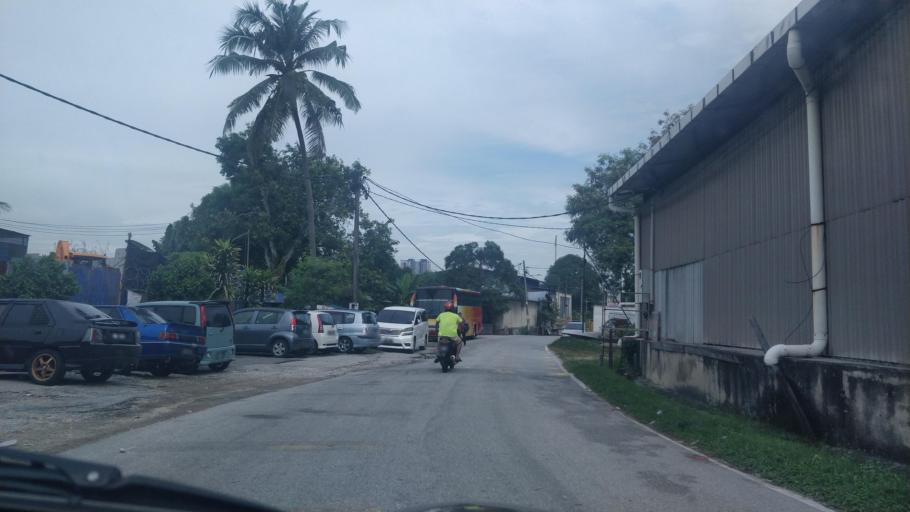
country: MY
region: Selangor
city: Kuang
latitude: 3.2015
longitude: 101.5941
